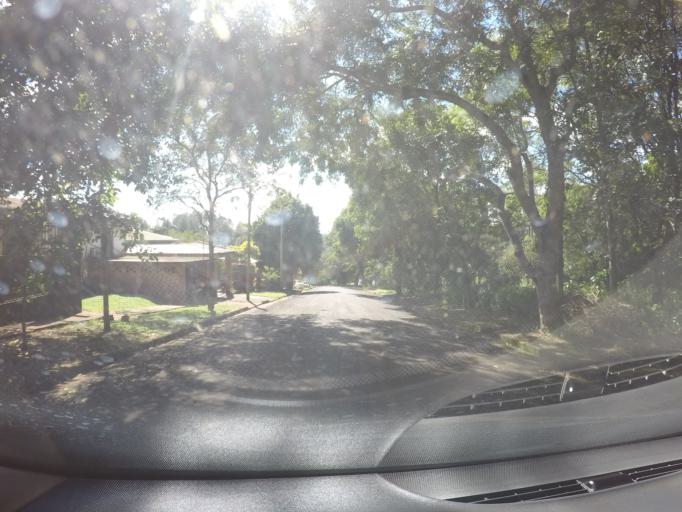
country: AR
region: Misiones
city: Puerto Rico
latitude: -26.8008
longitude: -55.0244
